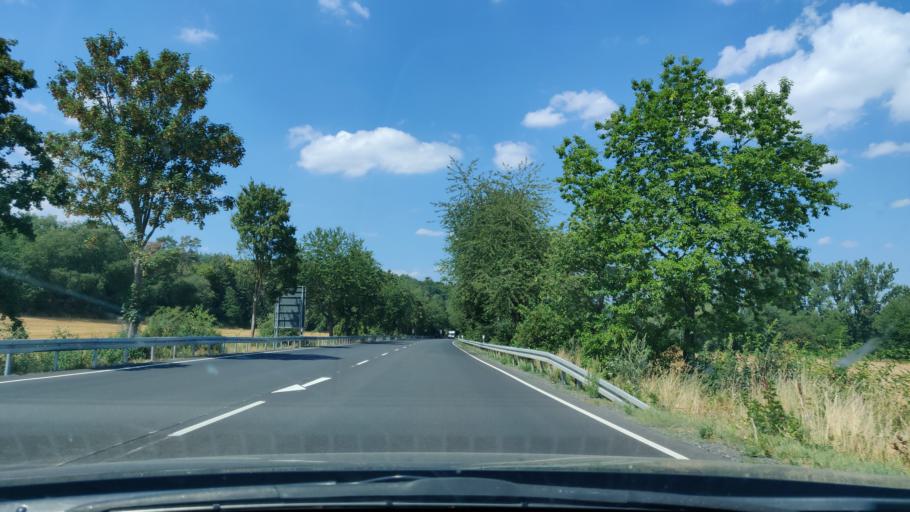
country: DE
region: Hesse
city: Fritzlar
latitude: 51.1169
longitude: 9.2547
